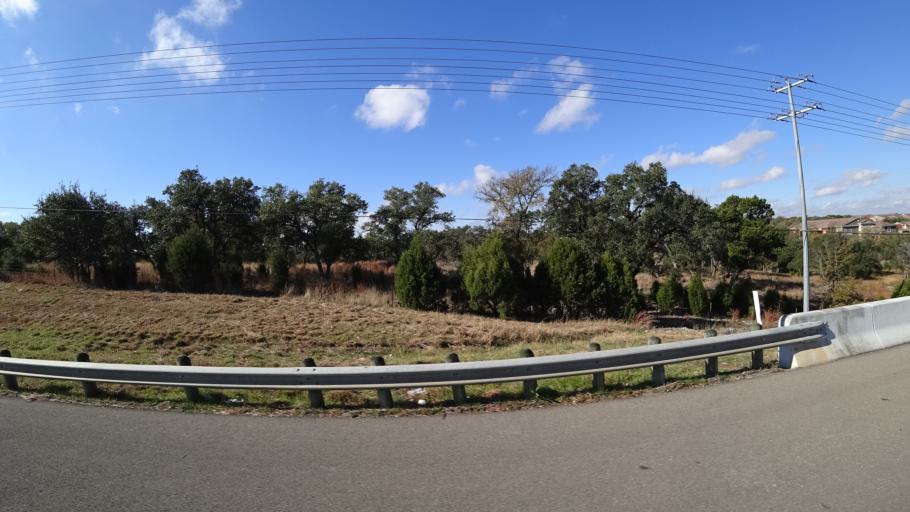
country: US
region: Texas
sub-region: Williamson County
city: Brushy Creek
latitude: 30.5271
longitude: -97.7770
